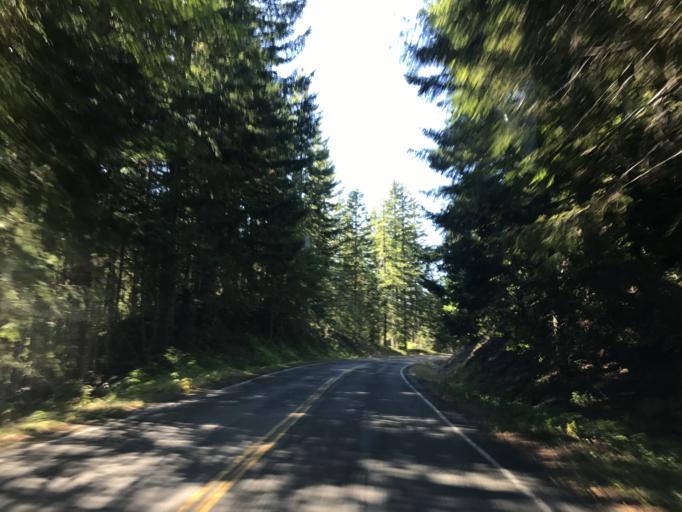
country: US
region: Washington
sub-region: Pierce County
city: Buckley
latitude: 46.7426
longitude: -121.6170
